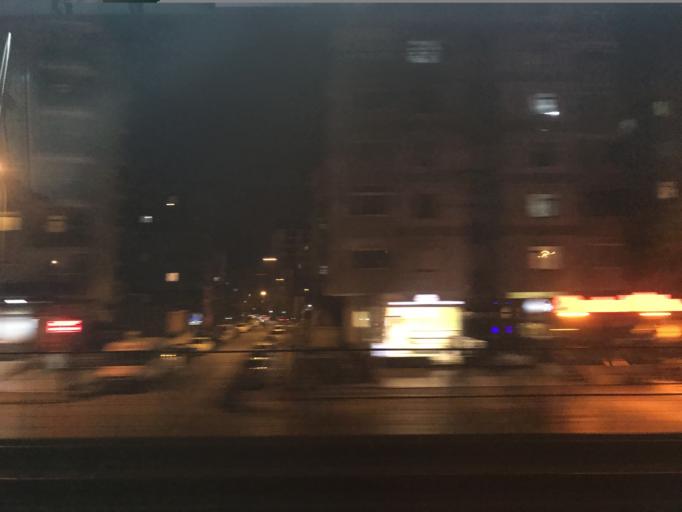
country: TR
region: Istanbul
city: Maltepe
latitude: 40.9038
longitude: 29.1637
